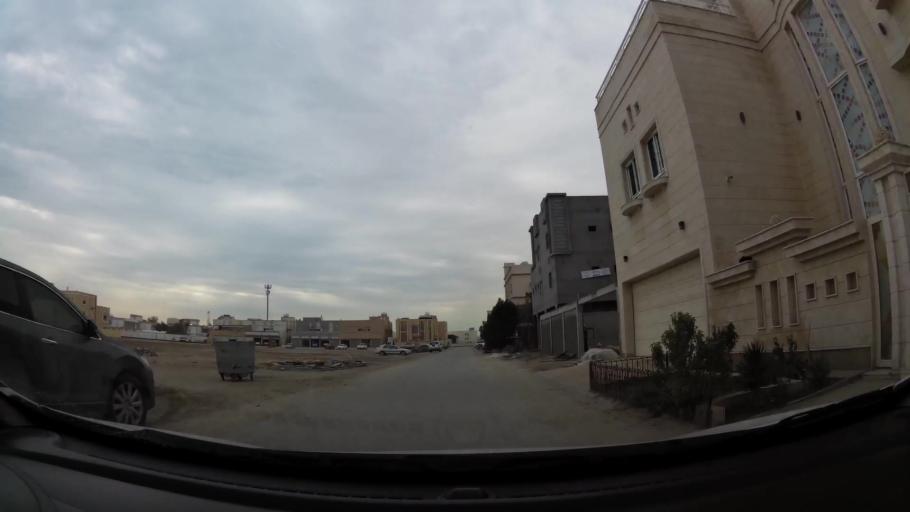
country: BH
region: Northern
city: Sitrah
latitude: 26.1712
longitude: 50.6058
